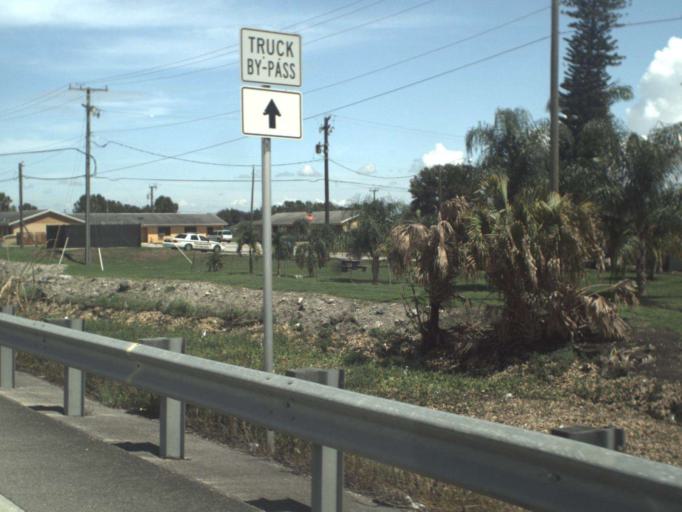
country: US
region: Florida
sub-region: Palm Beach County
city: Pahokee
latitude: 26.8067
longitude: -80.6533
